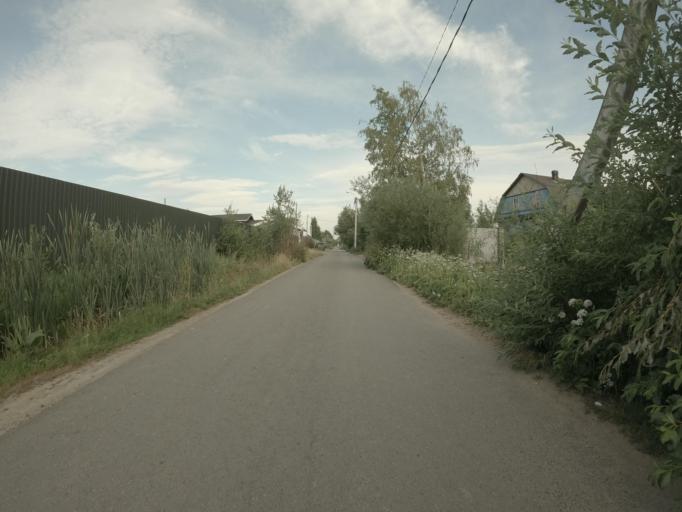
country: RU
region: St.-Petersburg
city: Krasnogvargeisky
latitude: 59.9380
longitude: 30.5093
